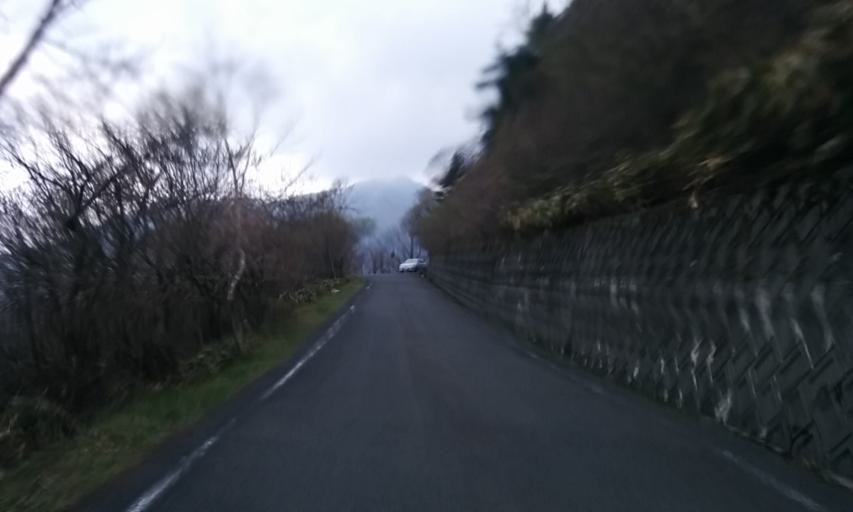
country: JP
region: Ehime
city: Saijo
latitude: 33.7889
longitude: 133.2088
